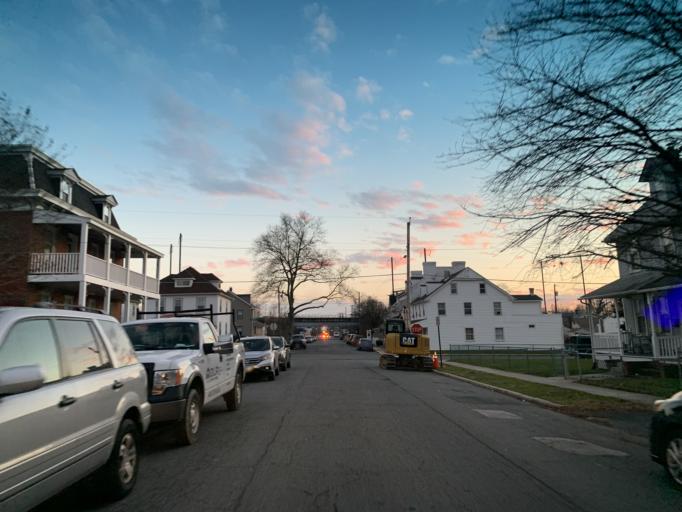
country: US
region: Maryland
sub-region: Harford County
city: Havre de Grace
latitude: 39.5532
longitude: -76.0954
